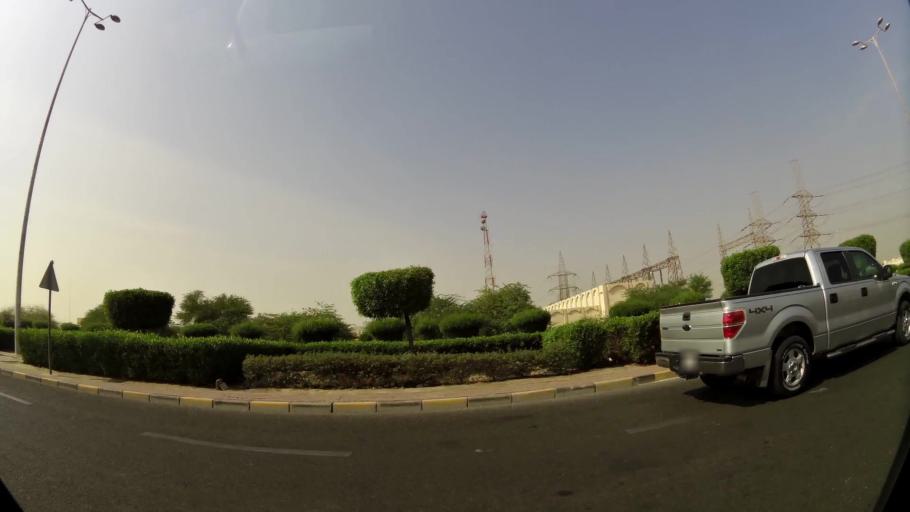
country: KW
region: Al Asimah
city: Ar Rabiyah
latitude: 29.2987
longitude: 47.9278
